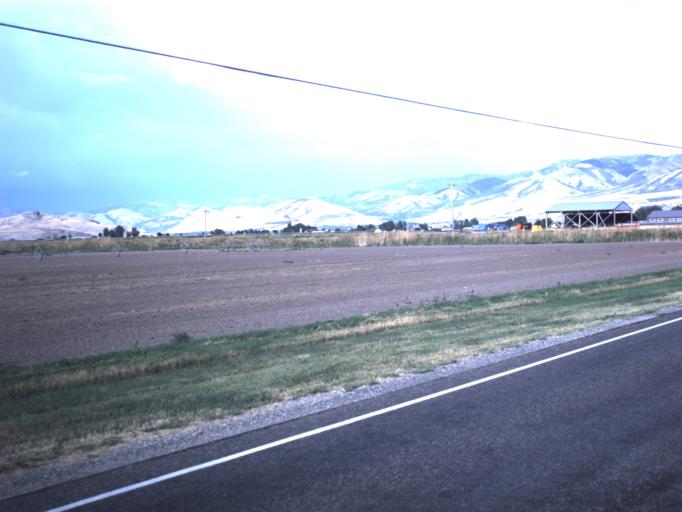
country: US
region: Utah
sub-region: Cache County
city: Lewiston
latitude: 41.9758
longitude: -111.8716
